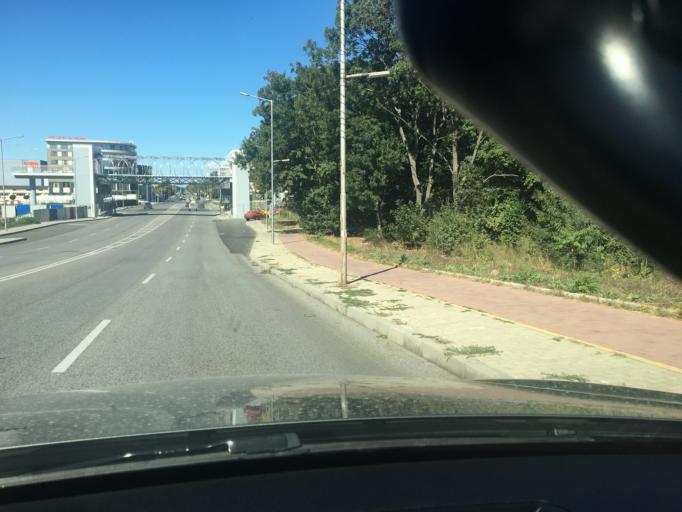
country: BG
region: Burgas
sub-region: Obshtina Burgas
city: Burgas
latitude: 42.5109
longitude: 27.4608
